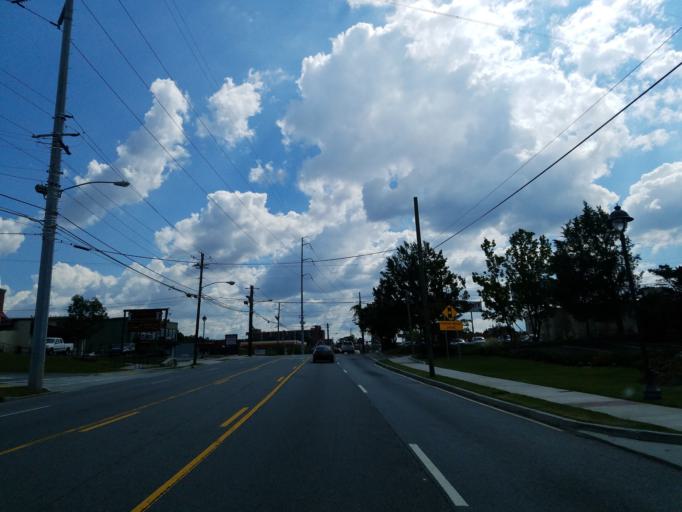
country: US
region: Georgia
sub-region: Fulton County
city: Sandy Springs
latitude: 33.9312
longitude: -84.3799
